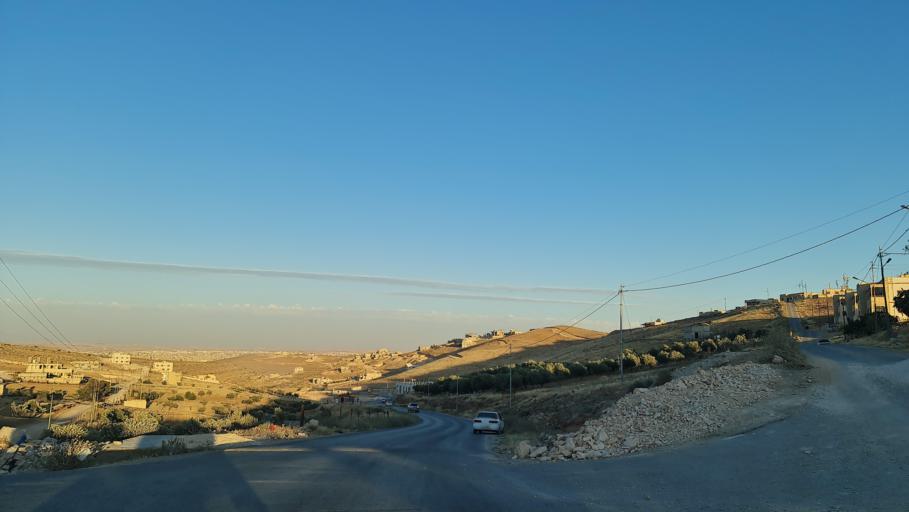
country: JO
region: Zarqa
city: Zarqa
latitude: 32.0873
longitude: 36.0236
